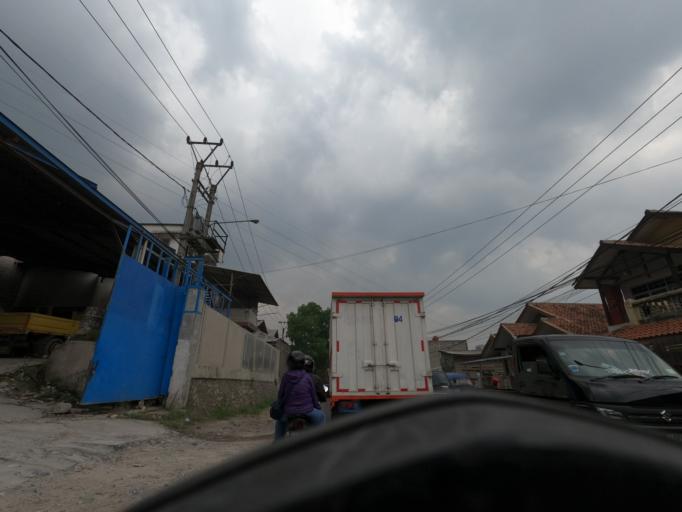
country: ID
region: West Java
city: Padalarang
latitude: -6.8323
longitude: 107.4608
